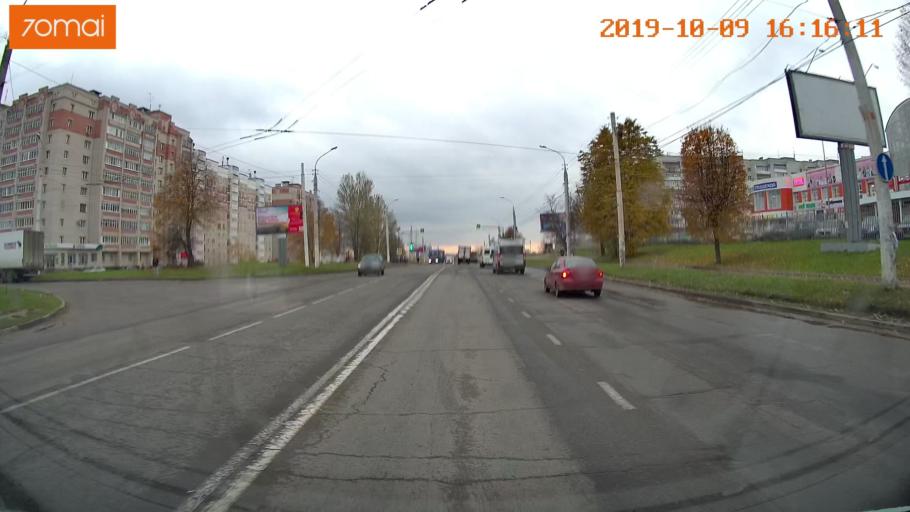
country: RU
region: Kostroma
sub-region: Kostromskoy Rayon
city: Kostroma
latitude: 57.7359
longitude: 40.9103
